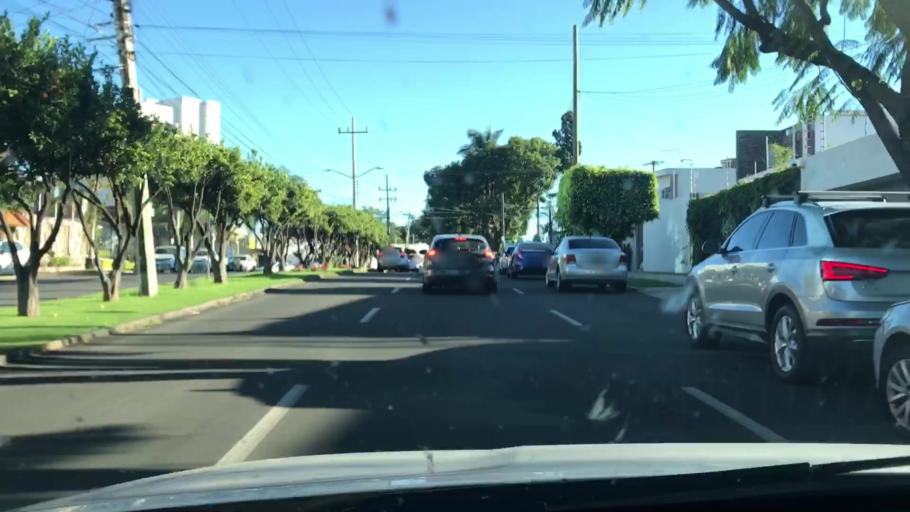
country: MX
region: Jalisco
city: Guadalajara
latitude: 20.6473
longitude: -103.4080
